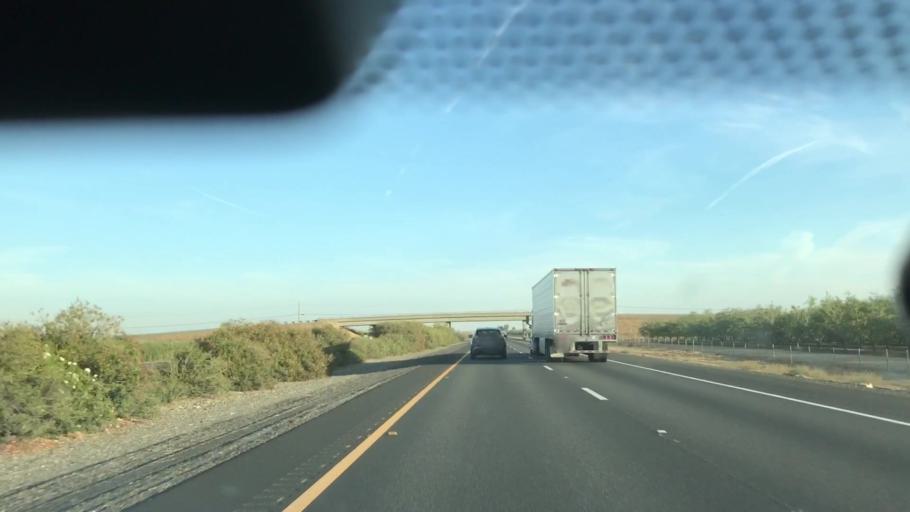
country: US
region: California
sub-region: Glenn County
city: Orland
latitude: 39.6659
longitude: -122.2046
